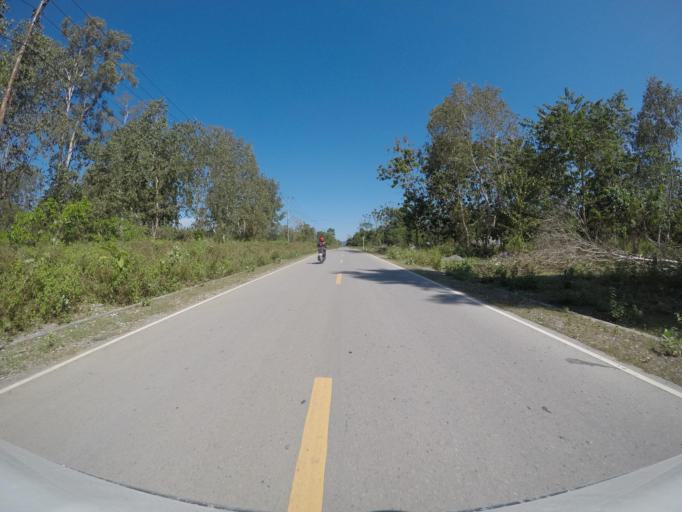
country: TL
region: Viqueque
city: Viqueque
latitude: -8.9762
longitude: 126.0405
